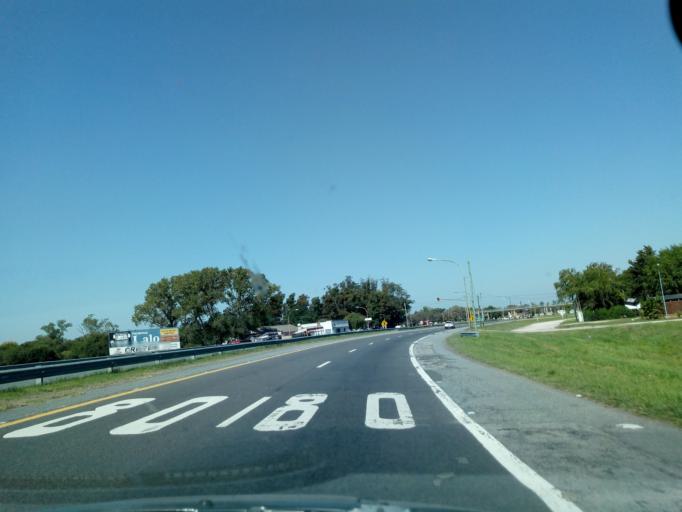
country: AR
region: Buenos Aires
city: Coronel Vidal
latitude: -37.2704
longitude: -57.7685
